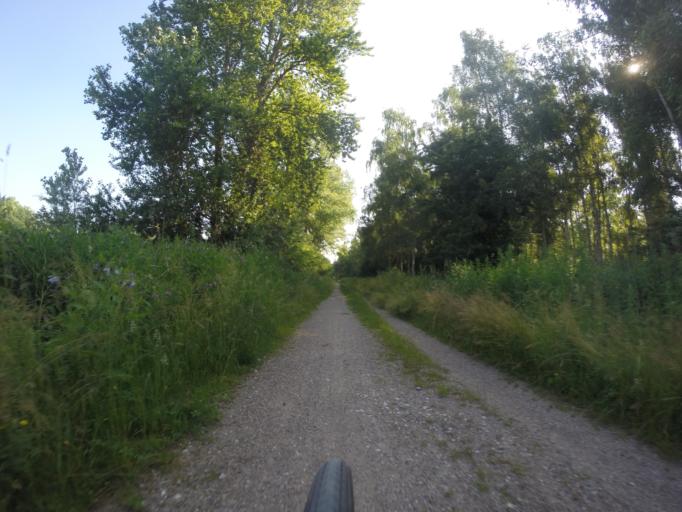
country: DK
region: Capital Region
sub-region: Ballerup Kommune
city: Ballerup
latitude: 55.6999
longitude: 12.3347
